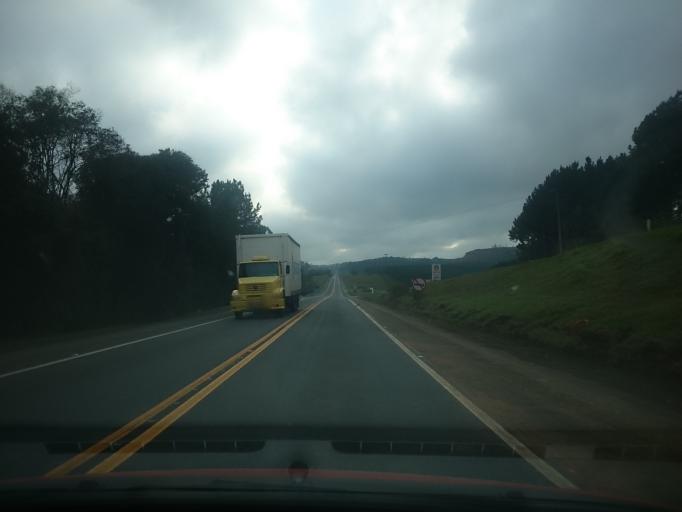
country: BR
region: Santa Catarina
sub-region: Lages
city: Lages
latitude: -27.8724
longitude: -50.4008
